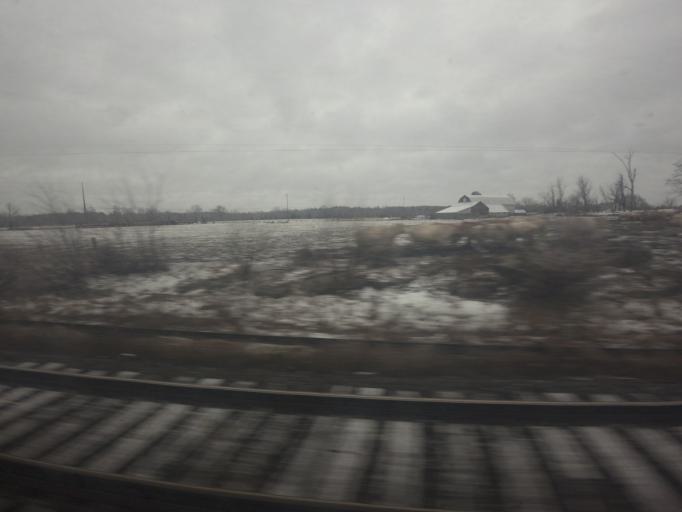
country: CA
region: Ontario
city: Gananoque
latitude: 44.3678
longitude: -76.1628
